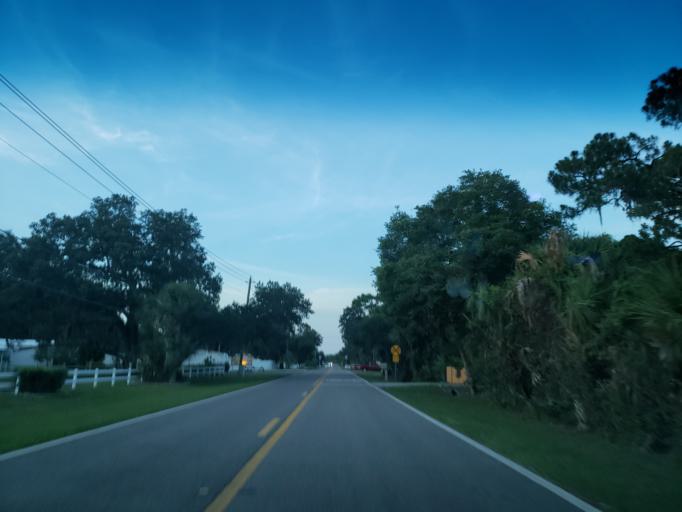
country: US
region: Florida
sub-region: Manatee County
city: Memphis
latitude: 27.5914
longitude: -82.5447
